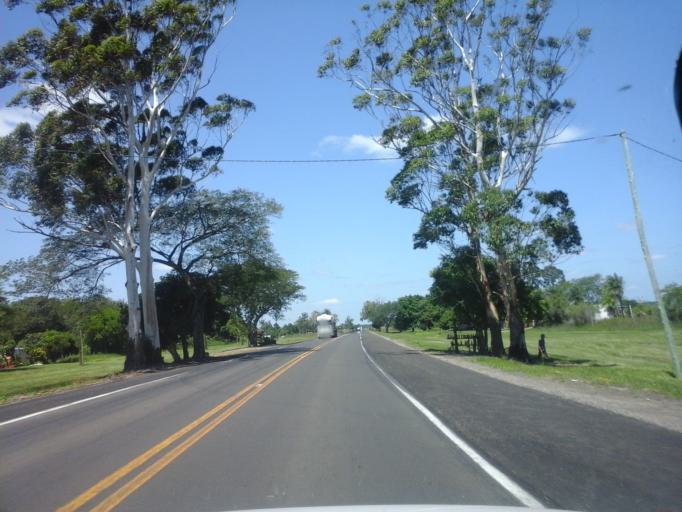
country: AR
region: Corrientes
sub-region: Departamento de Itati
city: Itati
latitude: -27.3575
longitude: -58.2603
